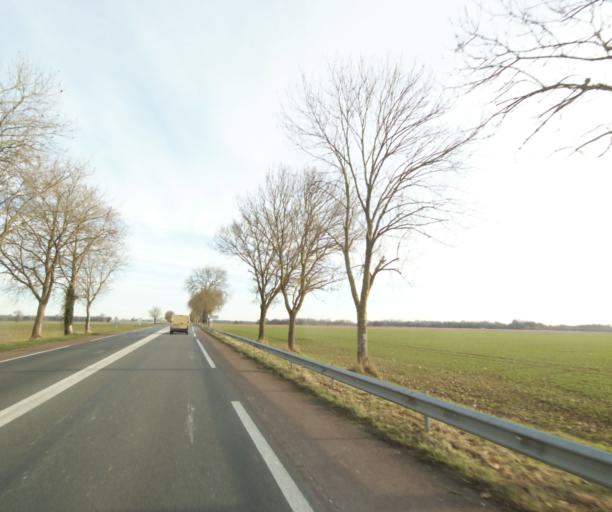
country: FR
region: Poitou-Charentes
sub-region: Departement de la Charente-Maritime
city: Saint-Porchaire
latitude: 45.8018
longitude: -0.7470
